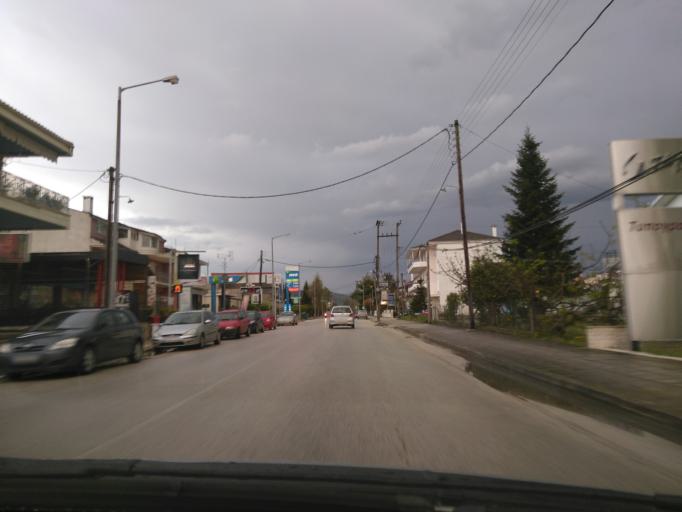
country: GR
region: Epirus
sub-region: Nomos Ioanninon
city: Katsikas
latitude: 39.6267
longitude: 20.8832
